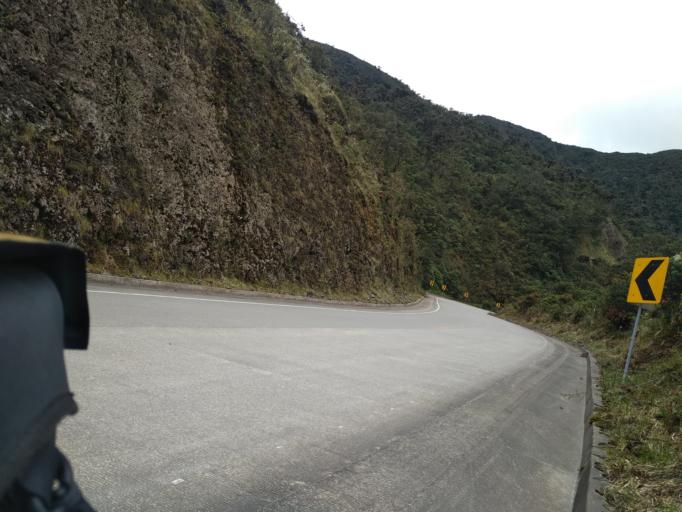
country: EC
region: Zamora-Chinchipe
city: Zamora
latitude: -4.4356
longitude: -79.1489
